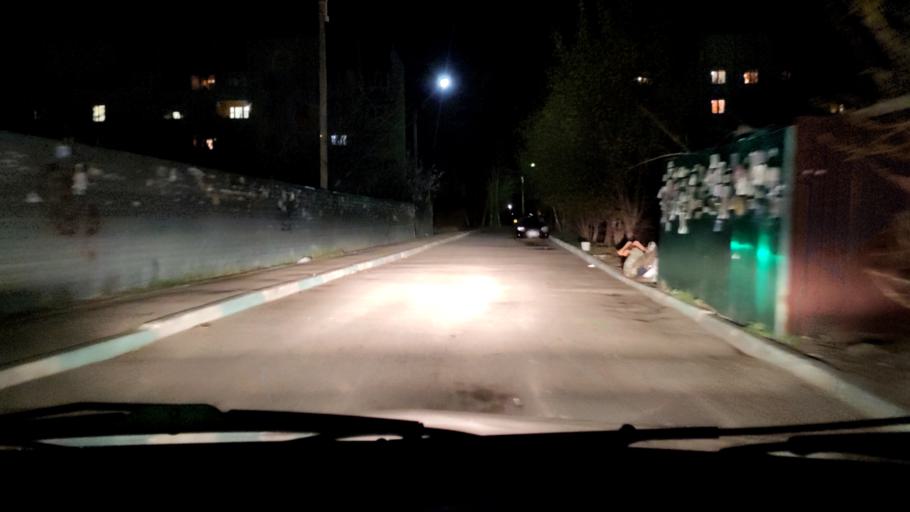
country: RU
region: Voronezj
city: Novaya Usman'
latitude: 51.6089
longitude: 39.3719
